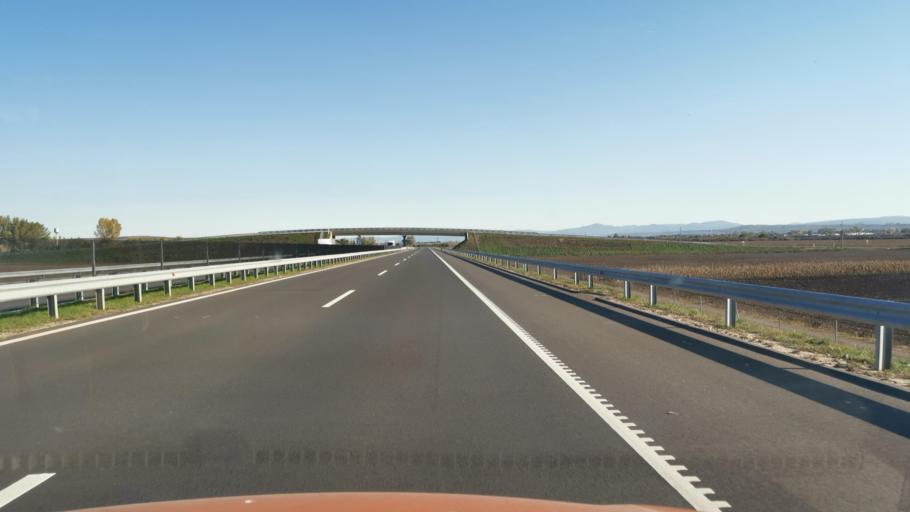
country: HU
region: Borsod-Abauj-Zemplen
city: Aszalo
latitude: 48.2371
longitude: 20.9619
